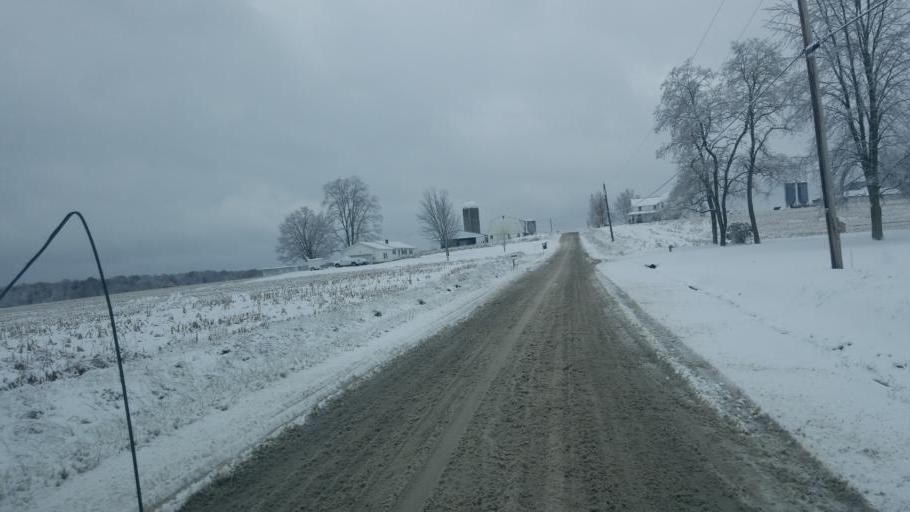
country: US
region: Ohio
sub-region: Geauga County
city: Middlefield
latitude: 41.4153
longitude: -81.0509
